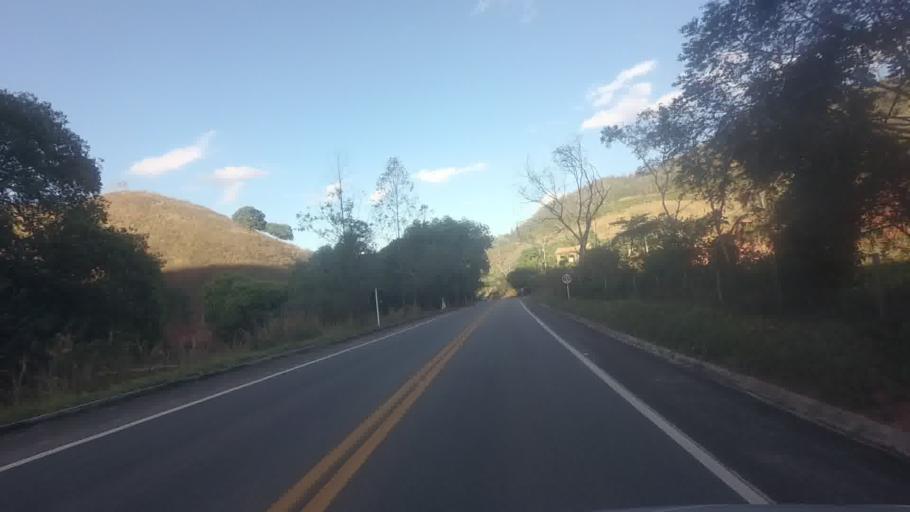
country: BR
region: Espirito Santo
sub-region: Cachoeiro De Itapemirim
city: Cachoeiro de Itapemirim
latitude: -20.8414
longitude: -41.2378
